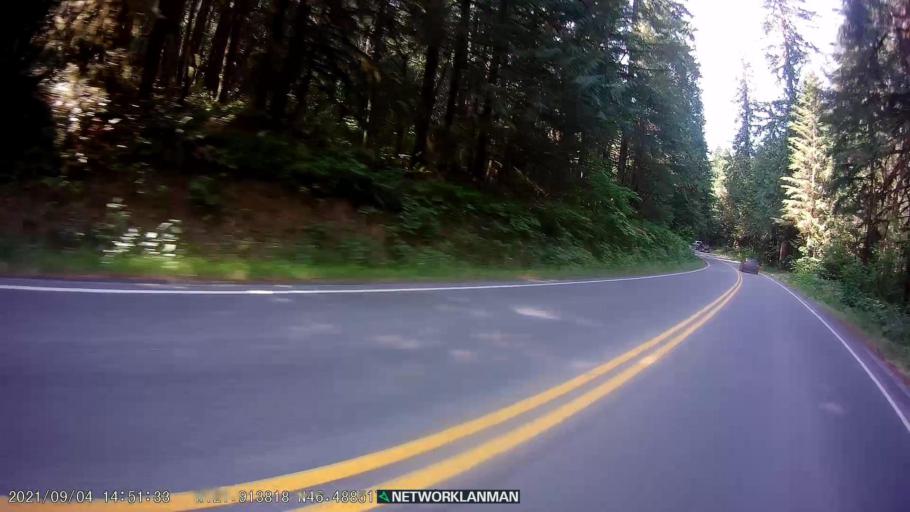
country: US
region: Washington
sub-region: Lewis County
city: Morton
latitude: 46.4887
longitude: -121.9140
